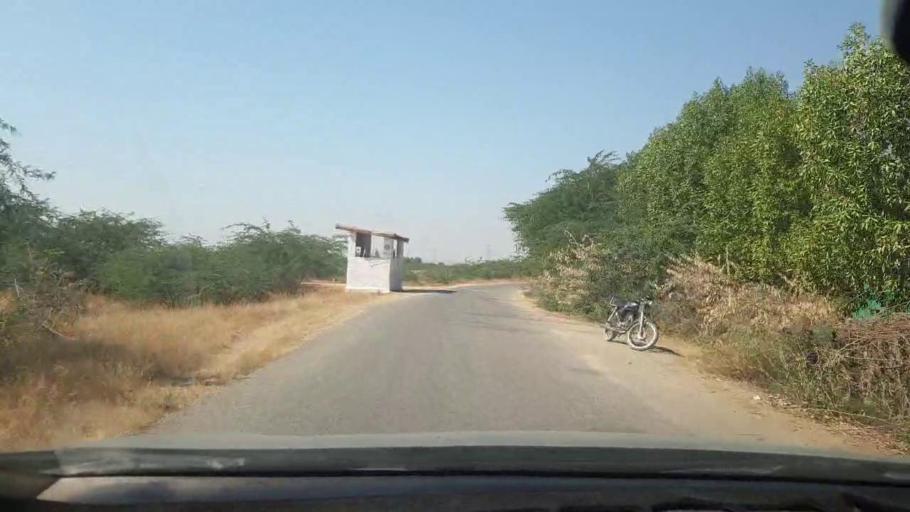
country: PK
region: Sindh
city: Malir Cantonment
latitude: 25.1618
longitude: 67.1555
